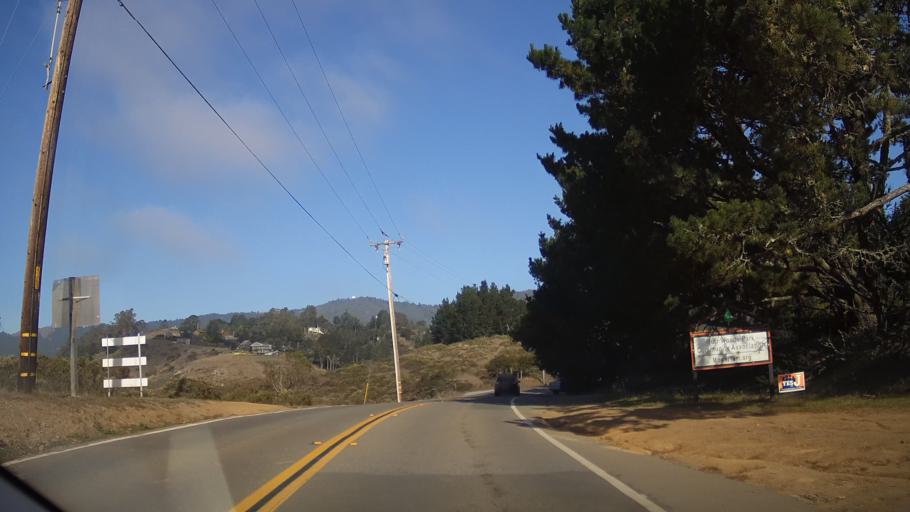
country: US
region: California
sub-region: Marin County
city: Mill Valley
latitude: 37.8938
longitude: -122.5579
